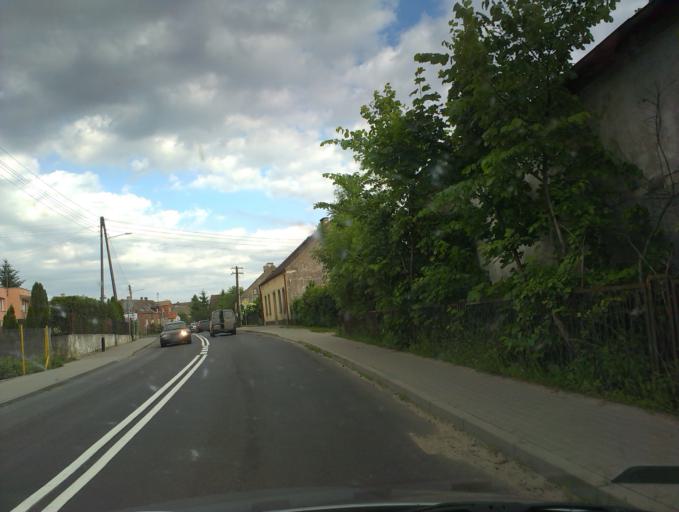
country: PL
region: West Pomeranian Voivodeship
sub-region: Powiat szczecinecki
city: Szczecinek
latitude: 53.6511
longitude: 16.6311
